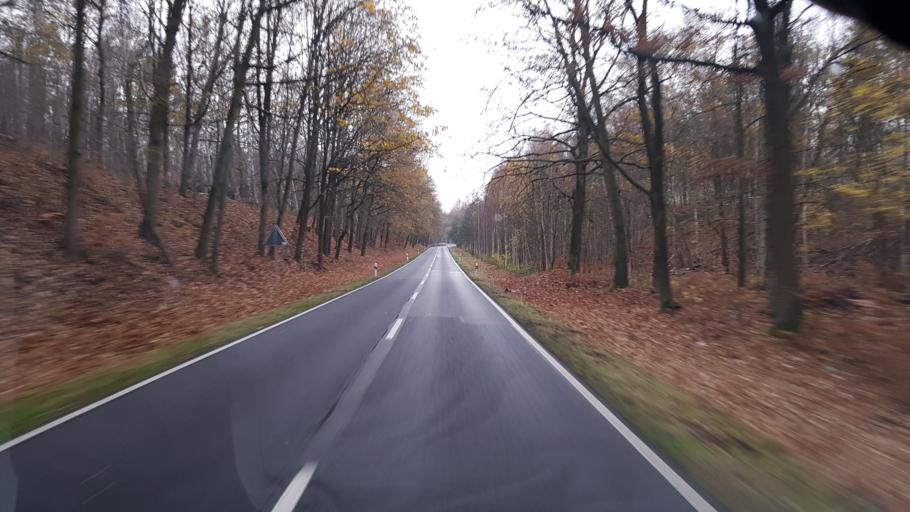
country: DE
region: Brandenburg
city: Lauchhammer
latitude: 51.5051
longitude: 13.7222
